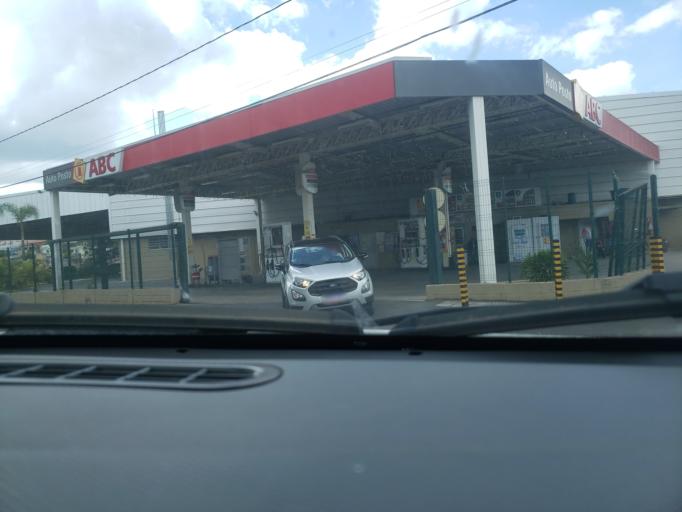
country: BR
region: Minas Gerais
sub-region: Campo Belo
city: Campo Belo
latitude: -20.8977
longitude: -45.2676
